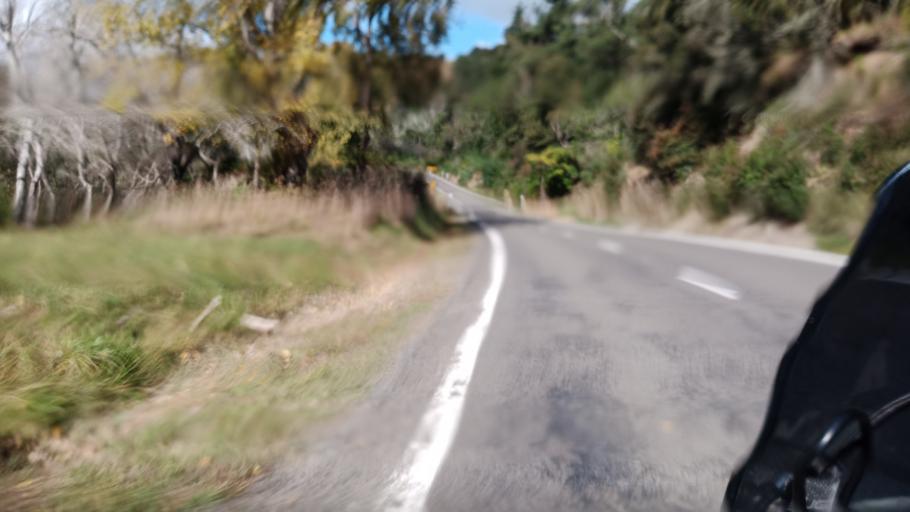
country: NZ
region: Gisborne
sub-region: Gisborne District
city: Gisborne
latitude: -38.4704
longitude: 177.6659
